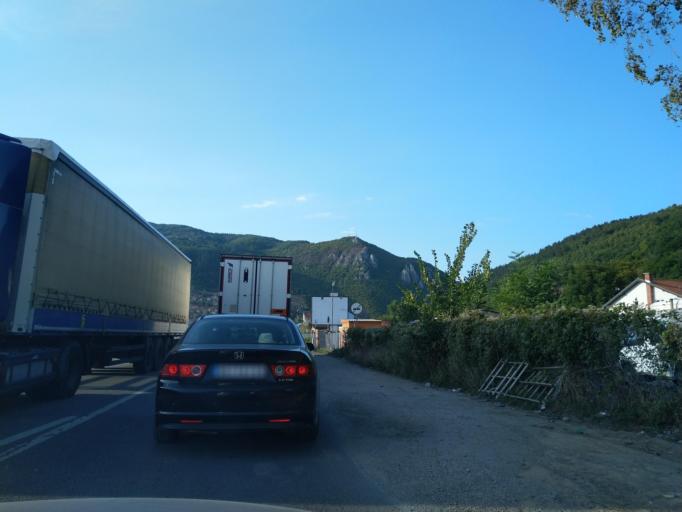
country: RS
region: Central Serbia
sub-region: Zlatiborski Okrug
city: Prijepolje
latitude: 43.3668
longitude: 19.6342
